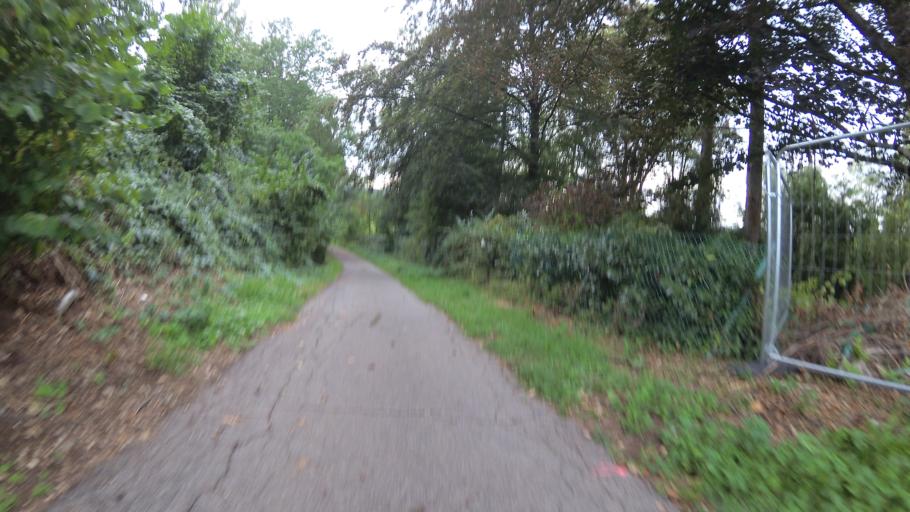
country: DE
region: Saarland
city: Homburg
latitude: 49.3075
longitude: 7.3079
